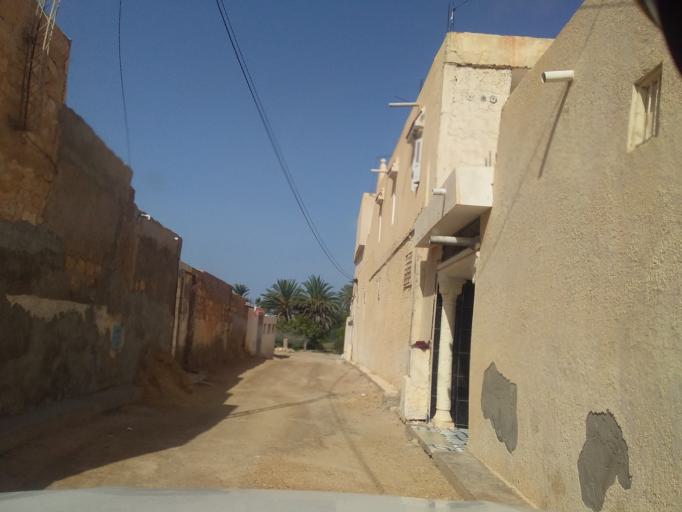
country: TN
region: Qabis
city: Gabes
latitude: 33.6301
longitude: 10.2876
